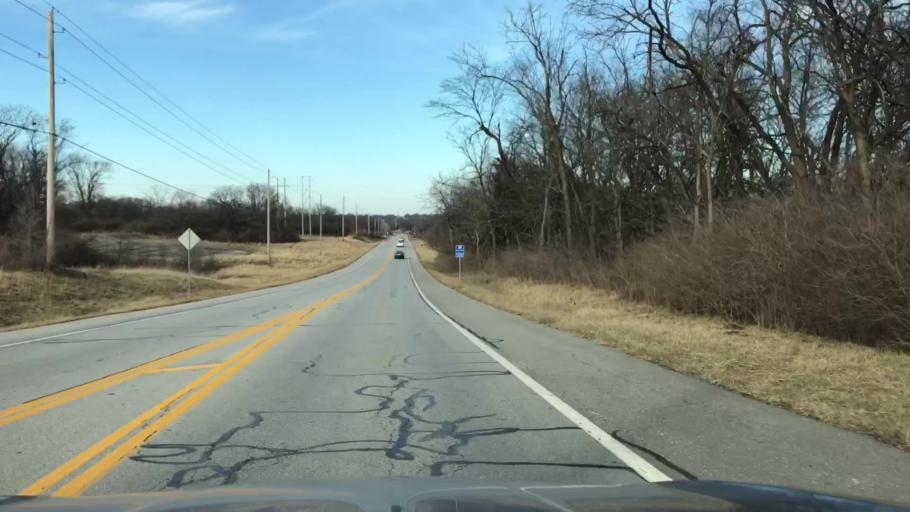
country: US
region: Missouri
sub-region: Jackson County
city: Lees Summit
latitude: 38.8910
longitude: -94.4149
